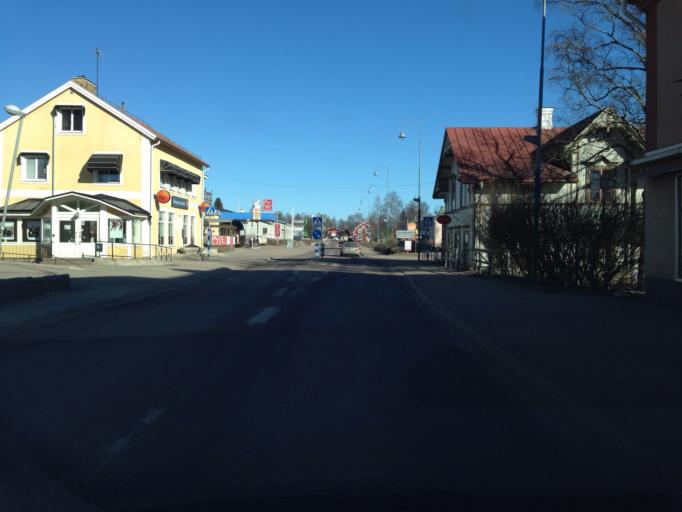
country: SE
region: Gaevleborg
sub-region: Ljusdals Kommun
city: Jaervsoe
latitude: 61.7154
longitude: 16.1696
